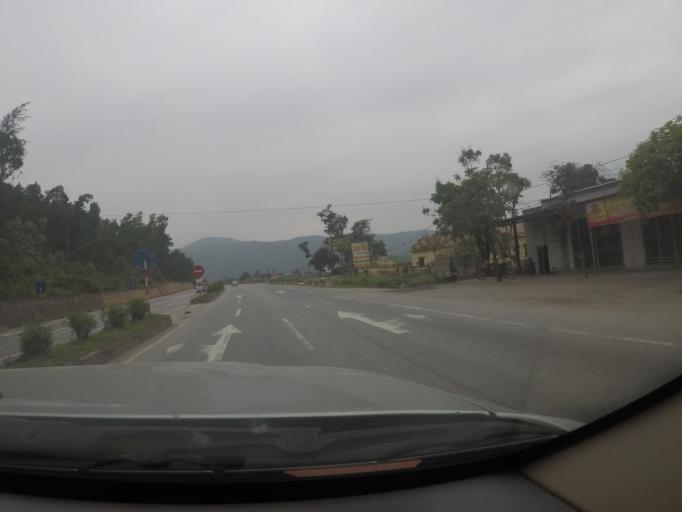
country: VN
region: Nghe An
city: Dien Chau
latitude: 18.8979
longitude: 105.6022
